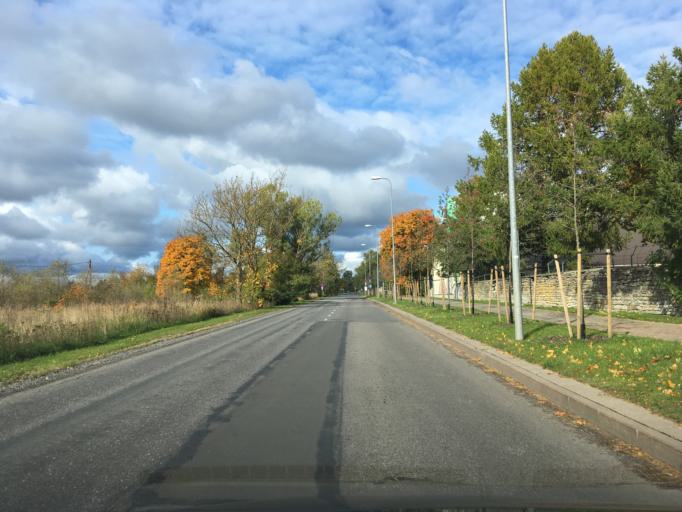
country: EE
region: Harju
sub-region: Tallinna linn
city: Kose
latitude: 59.4450
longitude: 24.8271
